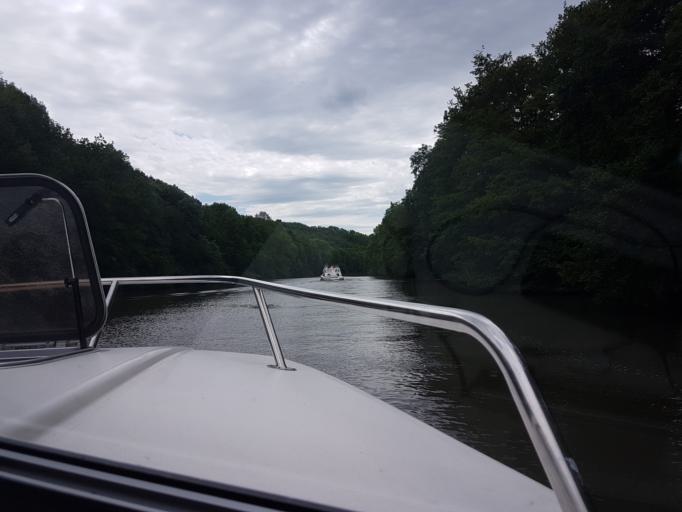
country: FR
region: Bourgogne
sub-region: Departement de la Nievre
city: Clamecy
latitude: 47.4726
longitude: 3.5278
